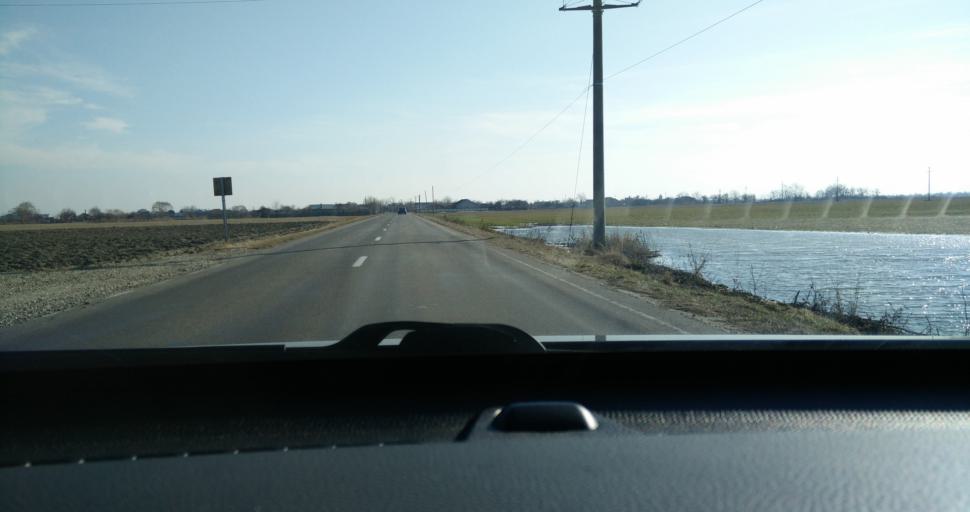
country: RO
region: Vrancea
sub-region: Comuna Nanesti
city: Nanesti
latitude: 45.5583
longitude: 27.4999
